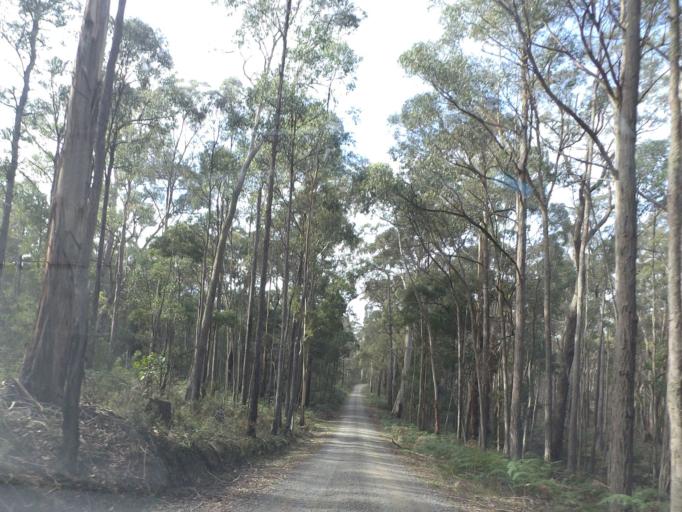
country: AU
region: Victoria
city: Brown Hill
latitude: -37.4923
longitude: 144.1747
